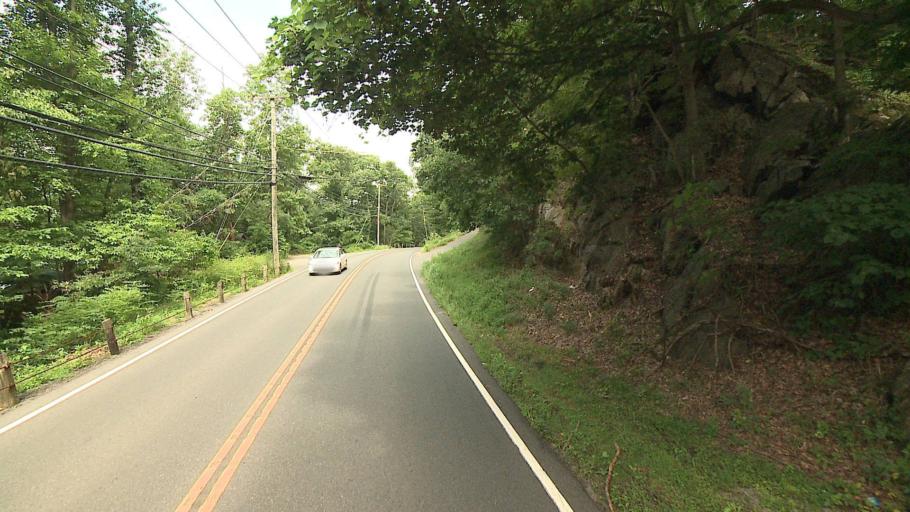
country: US
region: Connecticut
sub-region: Fairfield County
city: Sherman
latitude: 41.5127
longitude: -73.4722
